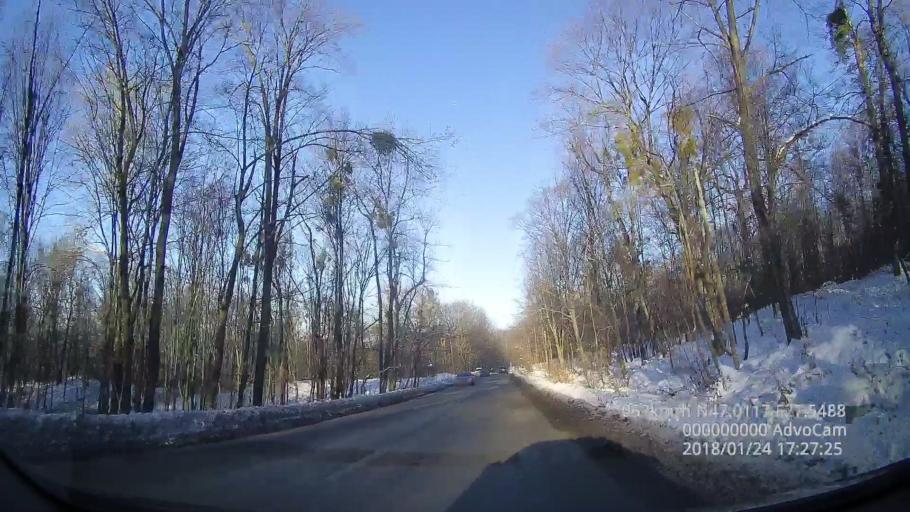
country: RO
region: Iasi
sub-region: Comuna Mogosesti
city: Mogosesti
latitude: 47.0120
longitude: 27.5492
